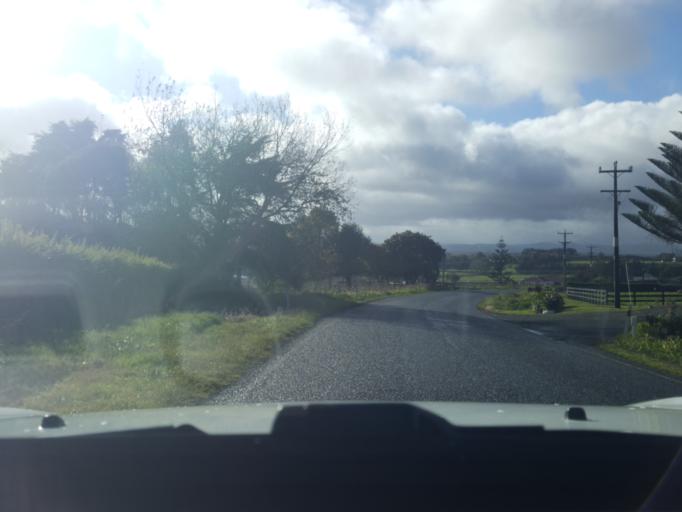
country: NZ
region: Auckland
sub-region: Auckland
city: Pukekohe East
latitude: -37.3078
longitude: 174.9974
